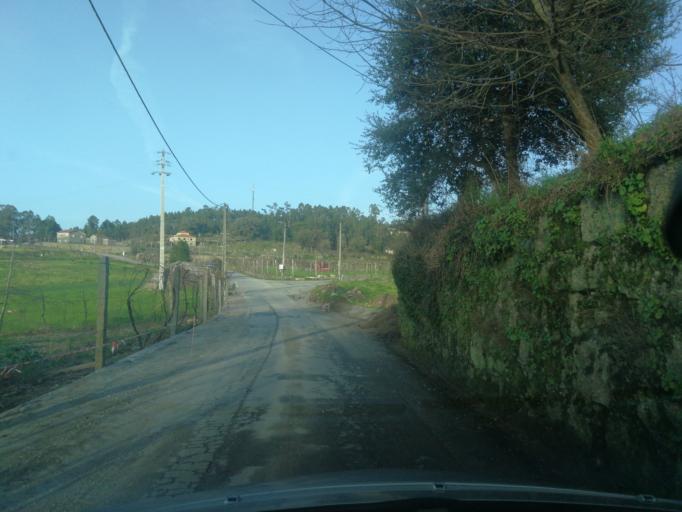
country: PT
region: Braga
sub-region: Barcelos
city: Galegos
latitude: 41.5194
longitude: -8.5513
